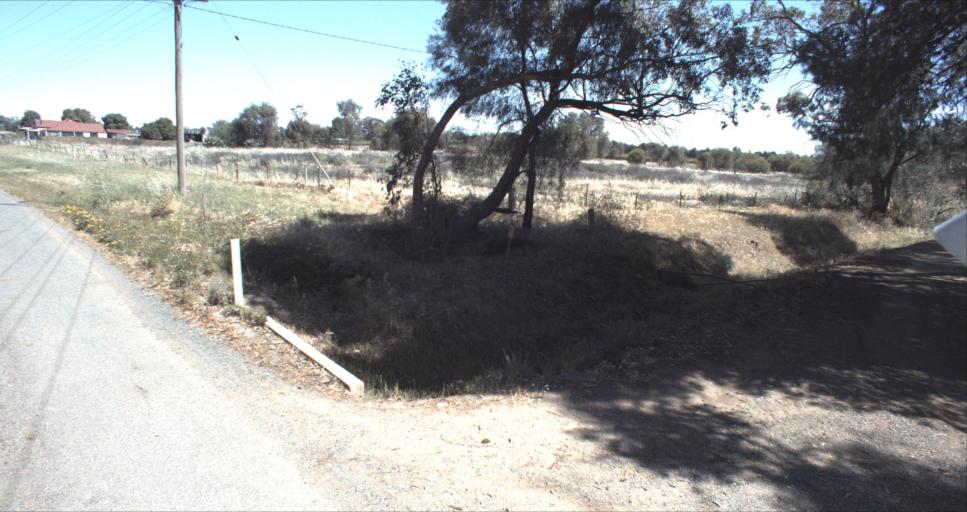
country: AU
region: New South Wales
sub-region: Leeton
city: Leeton
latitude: -34.5250
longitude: 146.3458
